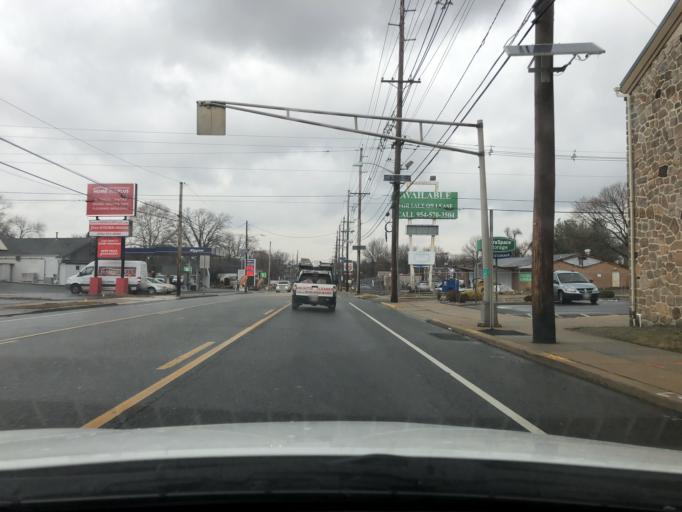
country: US
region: New Jersey
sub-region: Camden County
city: Bellmawr
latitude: 39.8695
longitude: -75.0808
